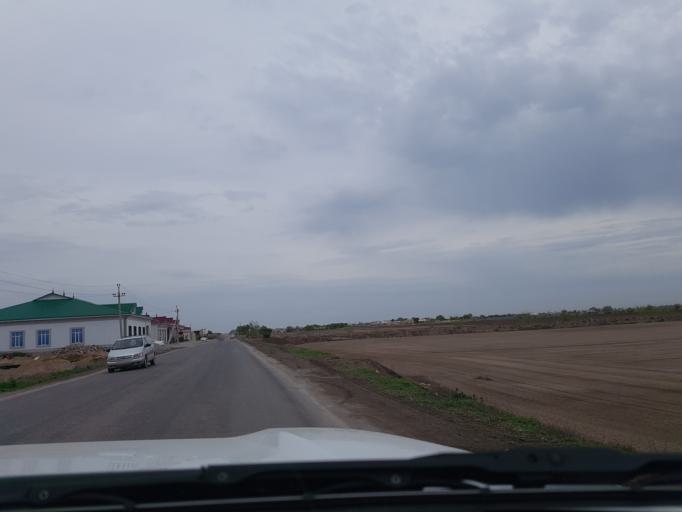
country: TM
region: Lebap
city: Turkmenabat
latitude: 39.0659
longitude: 63.5560
